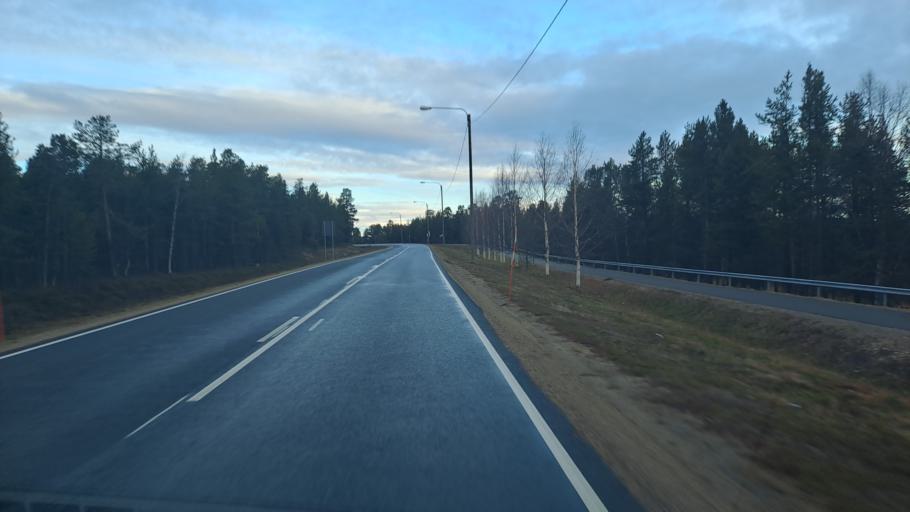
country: FI
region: Lapland
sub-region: Pohjois-Lappi
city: Inari
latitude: 68.8992
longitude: 27.0801
